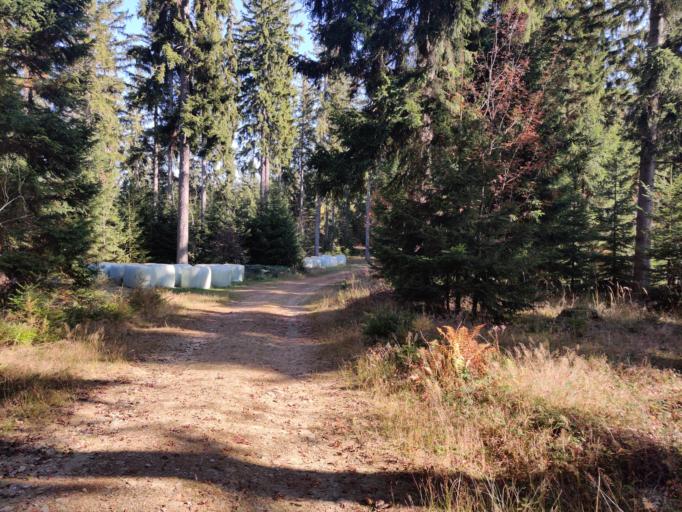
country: AT
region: Styria
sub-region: Politischer Bezirk Hartberg-Fuerstenfeld
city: Sankt Jakob im Walde
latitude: 47.4716
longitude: 15.8096
